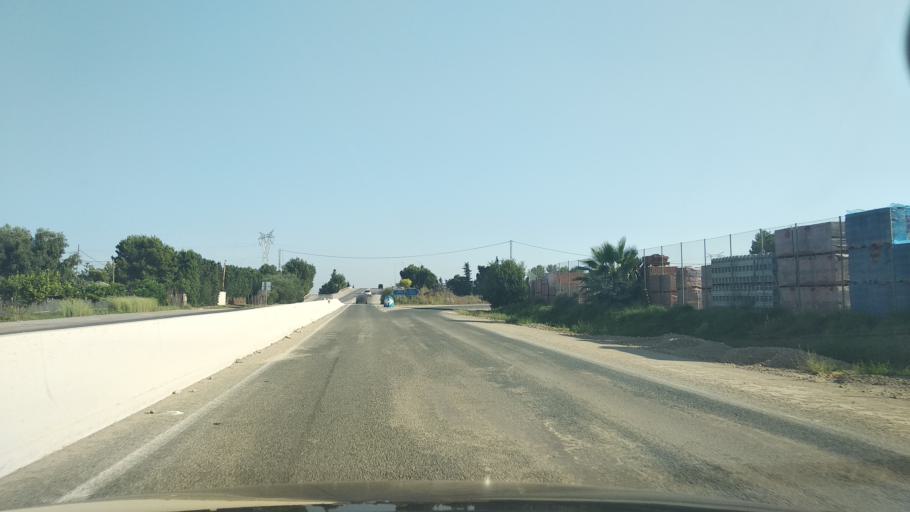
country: ES
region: Murcia
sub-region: Murcia
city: San Javier
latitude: 37.8179
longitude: -0.8456
